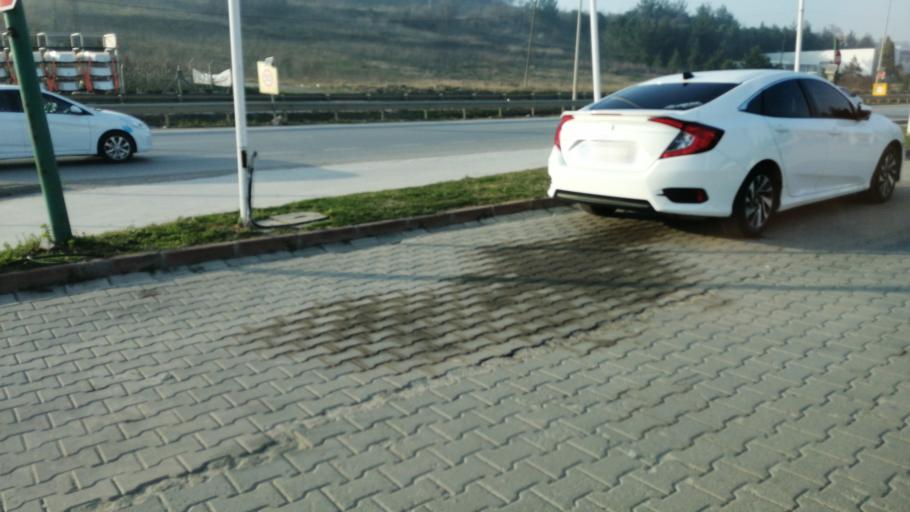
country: TR
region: Yalova
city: Yalova
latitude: 40.6249
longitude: 29.2713
